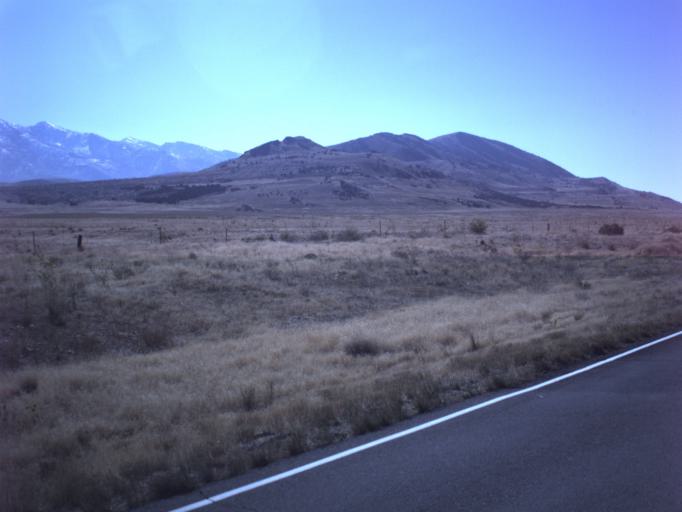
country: US
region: Utah
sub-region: Tooele County
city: Grantsville
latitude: 40.5901
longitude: -112.7209
